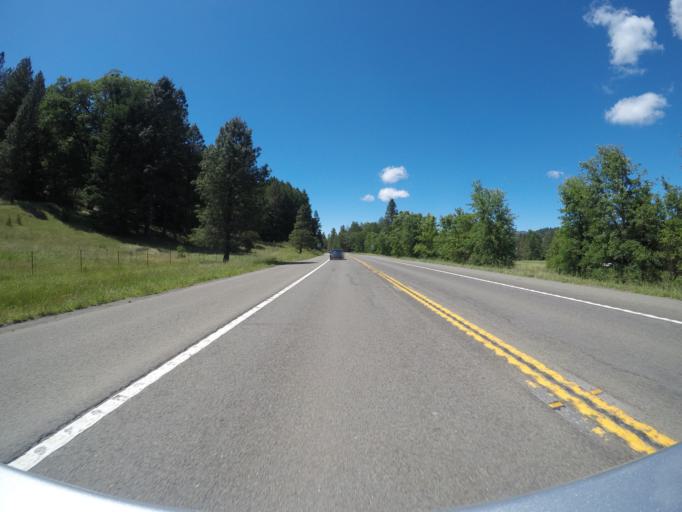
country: US
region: California
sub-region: Mendocino County
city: Laytonville
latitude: 39.7090
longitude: -123.4903
